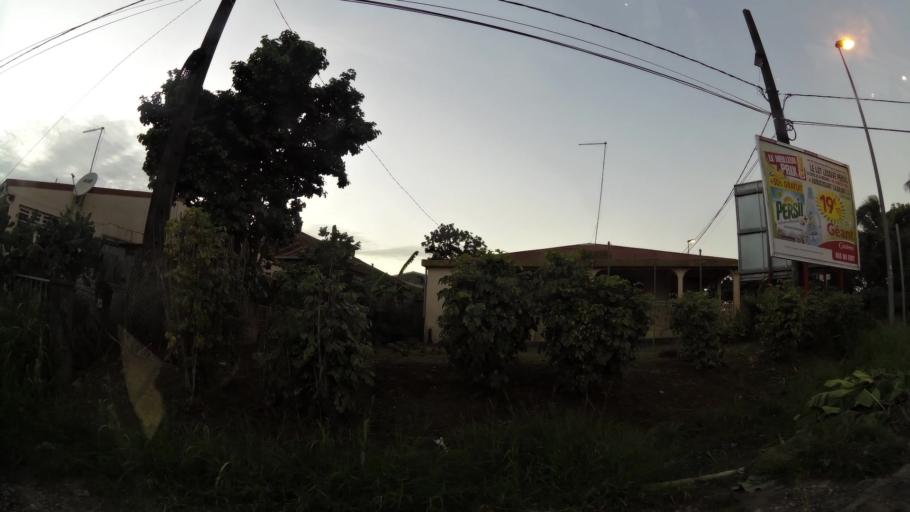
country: GP
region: Guadeloupe
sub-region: Guadeloupe
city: Les Abymes
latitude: 16.2758
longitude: -61.5076
